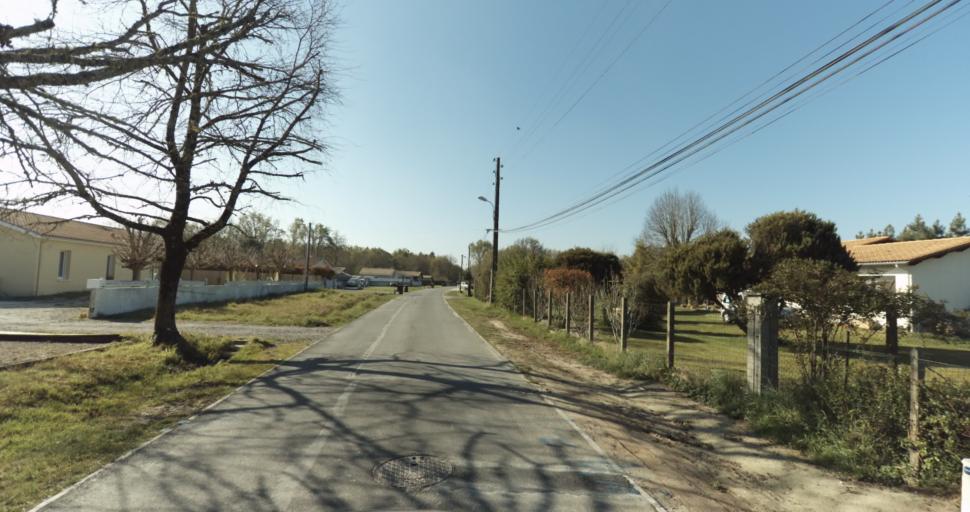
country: FR
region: Aquitaine
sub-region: Departement de la Gironde
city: Martignas-sur-Jalle
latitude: 44.8075
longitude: -0.8440
